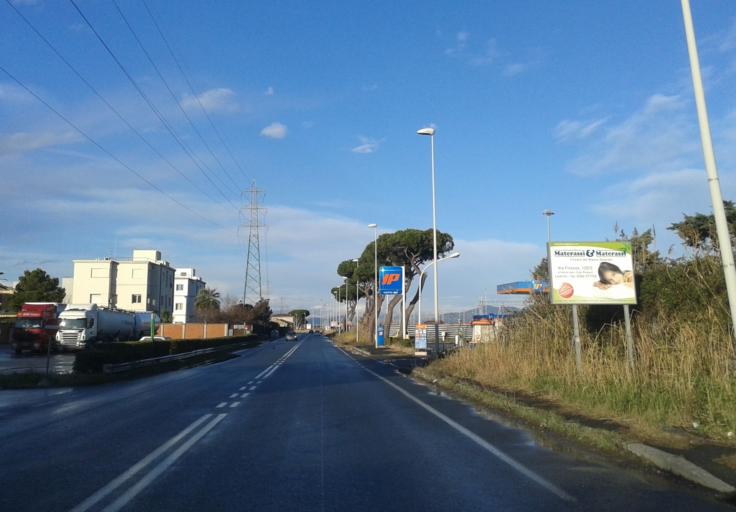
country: IT
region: Tuscany
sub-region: Provincia di Livorno
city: Livorno
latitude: 43.5734
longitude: 10.3196
